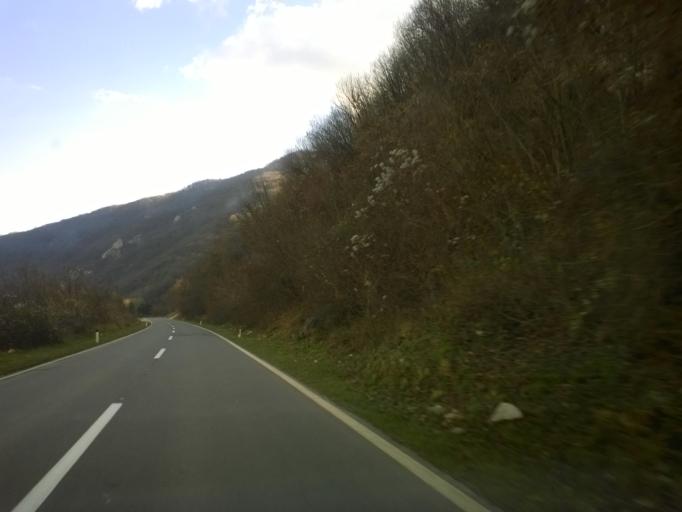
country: RO
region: Caras-Severin
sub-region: Comuna Pescari
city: Coronini
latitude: 44.6565
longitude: 21.7055
